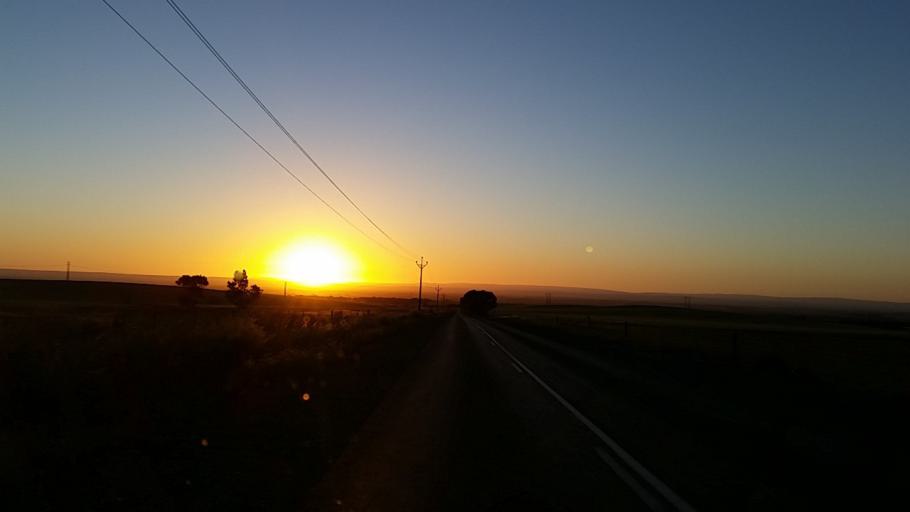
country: AU
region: South Australia
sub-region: Clare and Gilbert Valleys
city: Clare
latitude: -33.8394
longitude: 138.5353
